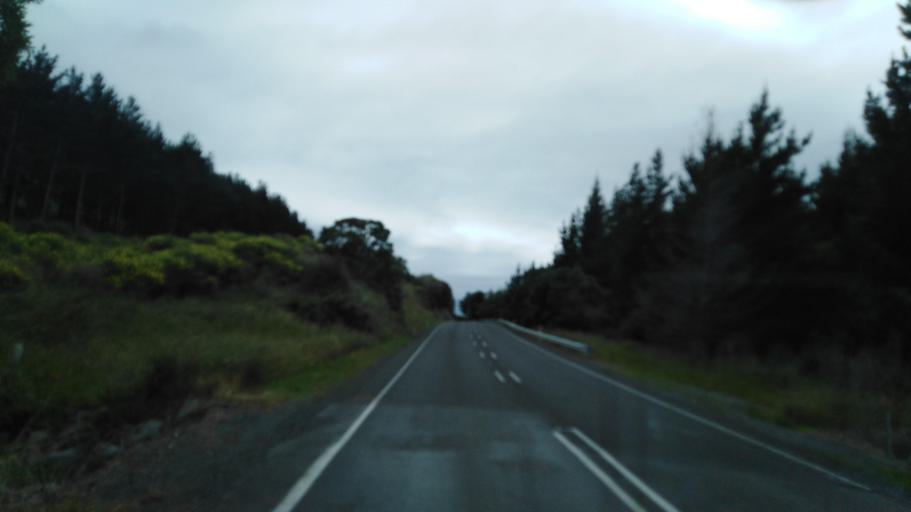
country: NZ
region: Canterbury
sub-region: Kaikoura District
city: Kaikoura
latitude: -42.1766
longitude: 173.9014
